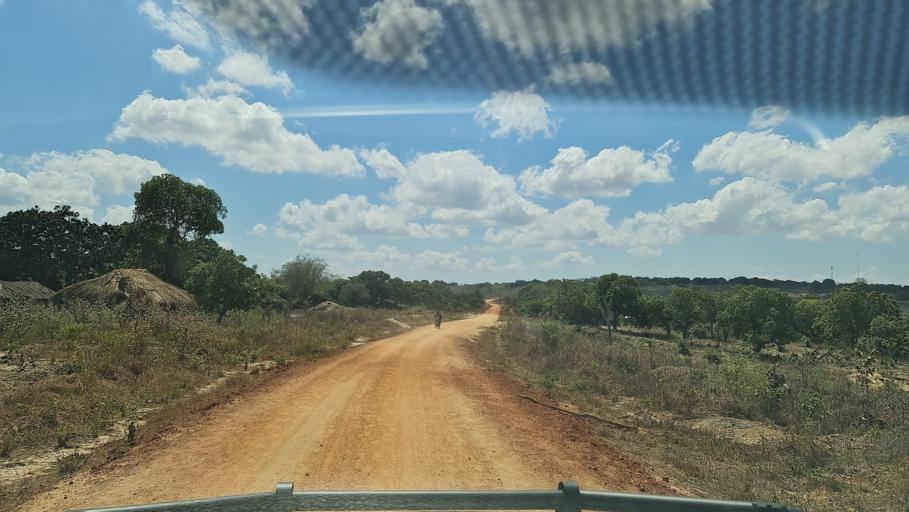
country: MZ
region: Nampula
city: Nacala
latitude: -14.1691
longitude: 40.2490
